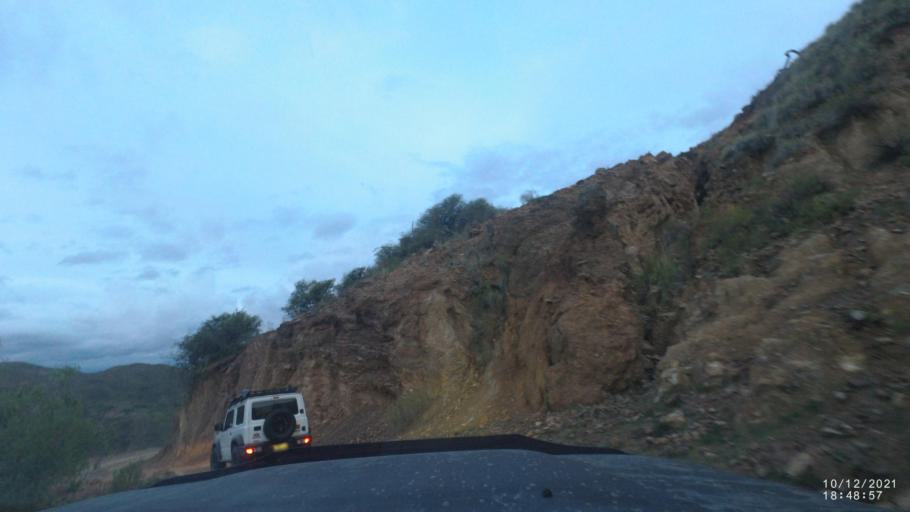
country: BO
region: Cochabamba
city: Tarata
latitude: -17.8819
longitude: -65.9727
